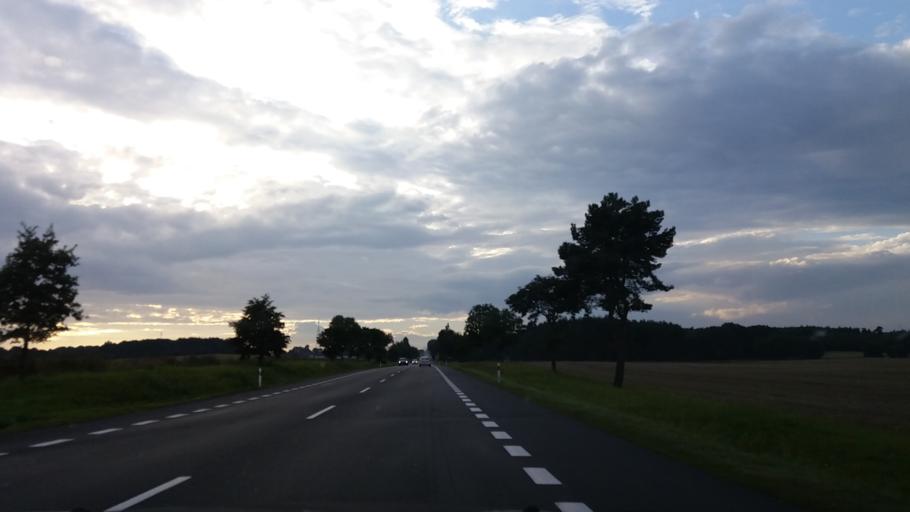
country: PL
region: Lower Silesian Voivodeship
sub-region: Powiat polkowicki
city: Gaworzyce
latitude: 51.6547
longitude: 15.8414
